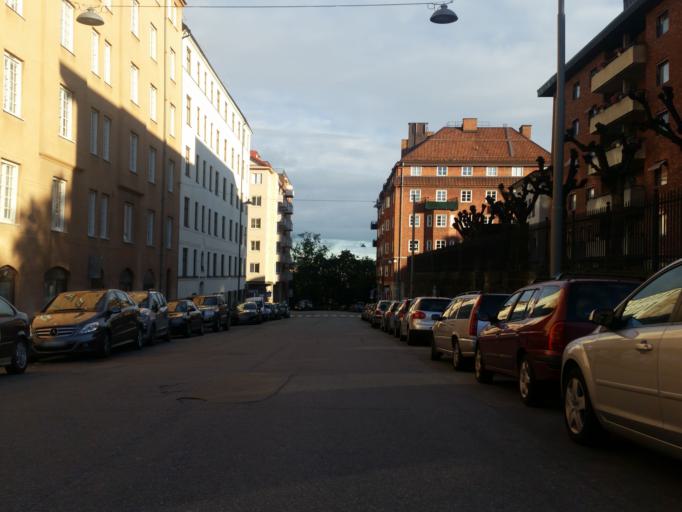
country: SE
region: Stockholm
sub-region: Stockholms Kommun
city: Arsta
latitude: 59.3186
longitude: 18.0396
